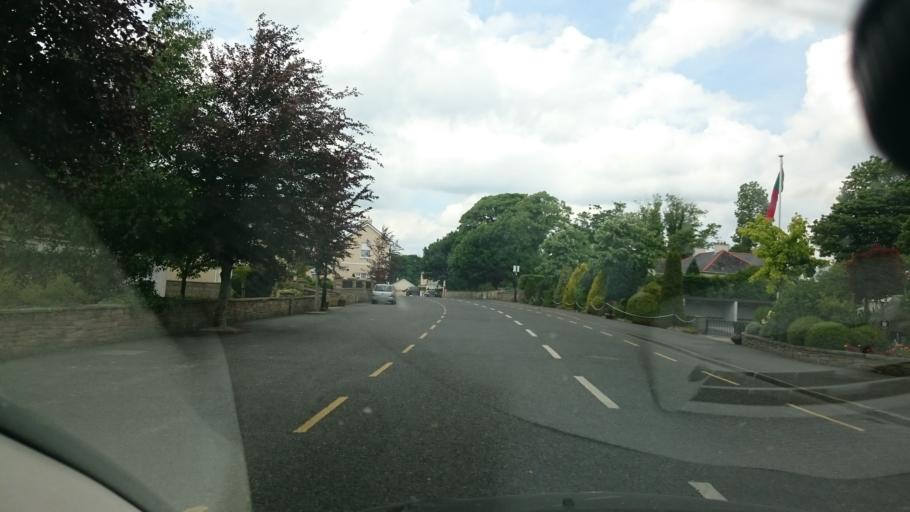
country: IE
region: Connaught
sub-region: Sligo
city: Inishcrone
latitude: 54.1096
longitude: -9.0263
